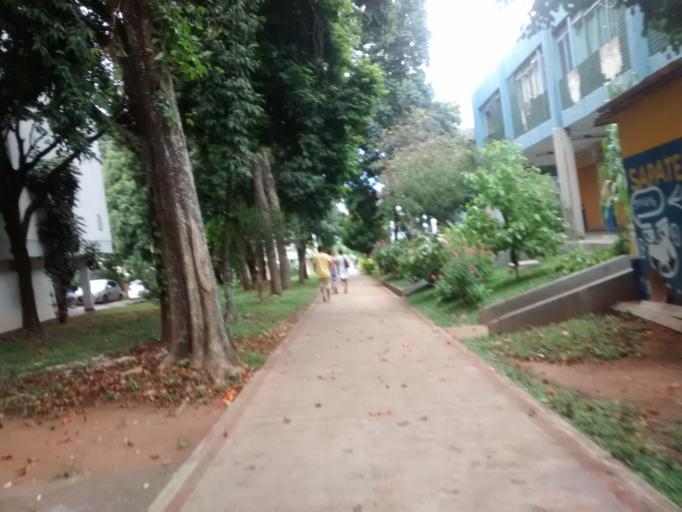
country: BR
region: Federal District
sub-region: Brasilia
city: Brasilia
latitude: -15.7660
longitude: -47.8780
